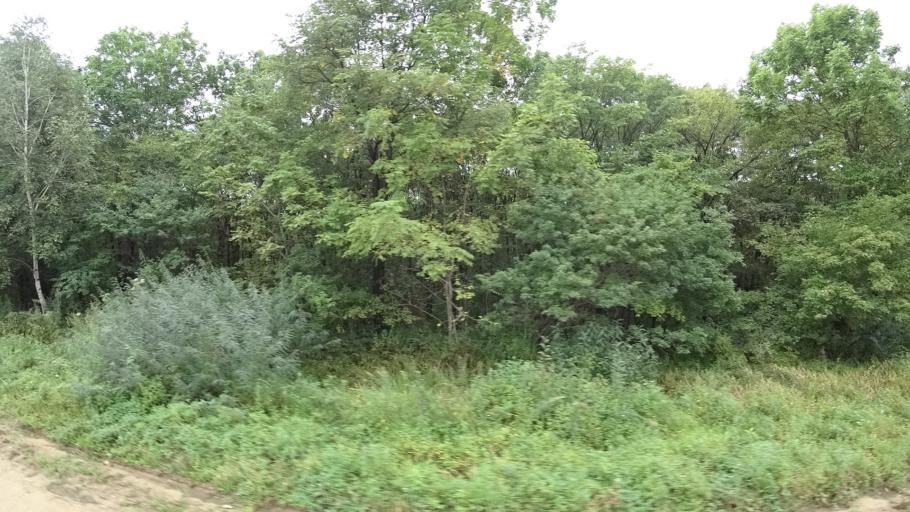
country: RU
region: Primorskiy
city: Rettikhovka
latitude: 44.0614
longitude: 132.6541
